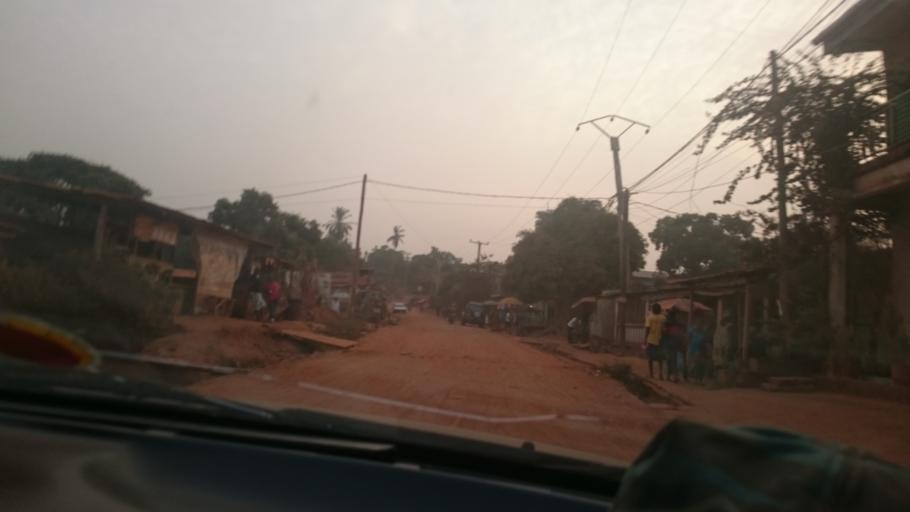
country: CM
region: Centre
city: Yaounde
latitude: 3.8183
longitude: 11.5051
